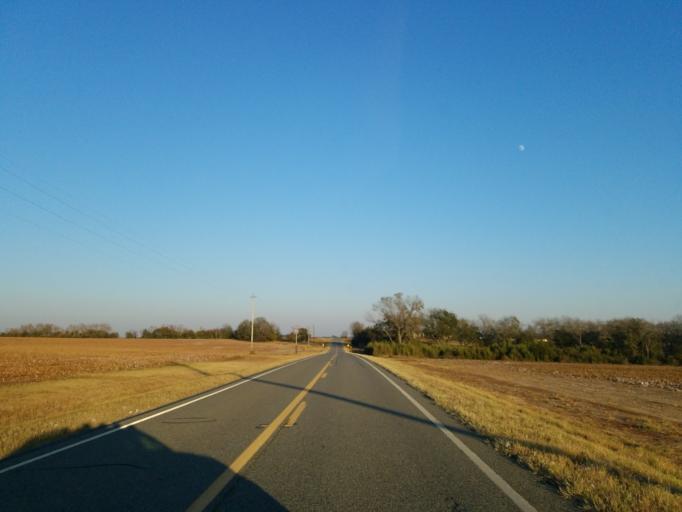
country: US
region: Georgia
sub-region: Turner County
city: Ashburn
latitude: 31.8596
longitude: -83.6052
